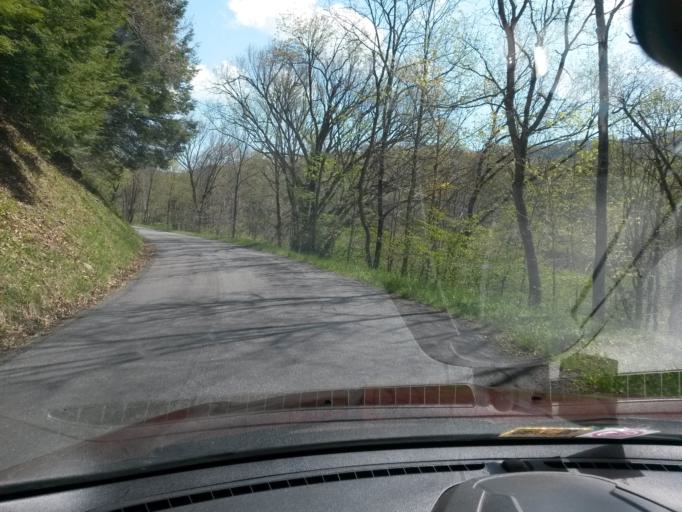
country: US
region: Virginia
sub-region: Highland County
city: Monterey
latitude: 38.2201
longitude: -79.6694
